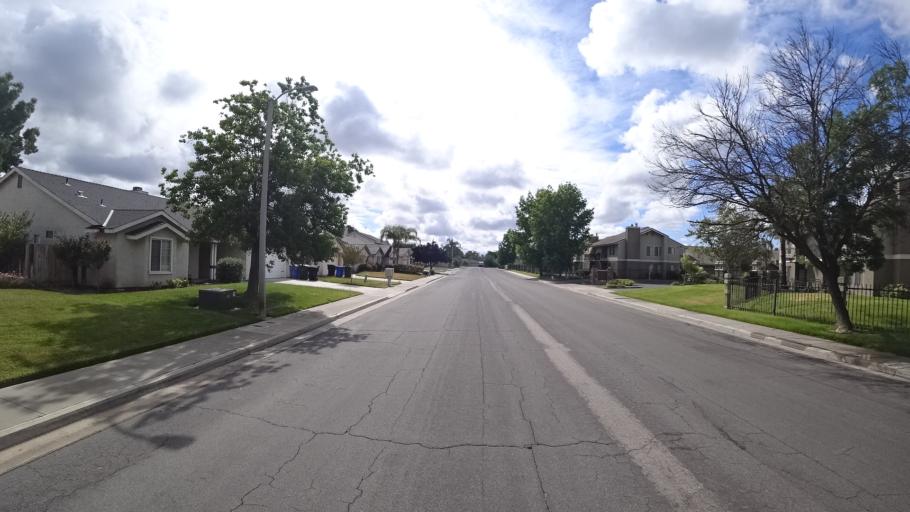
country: US
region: California
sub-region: Kings County
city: Lucerne
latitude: 36.3630
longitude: -119.6519
